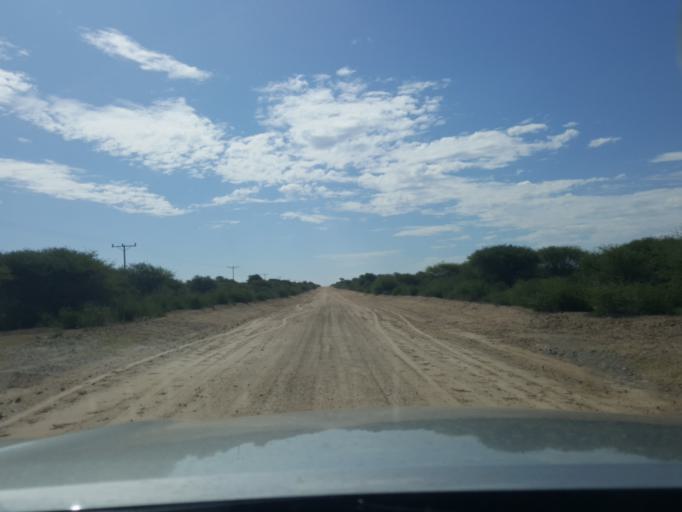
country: BW
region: Kweneng
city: Khudumelapye
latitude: -23.8786
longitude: 24.9049
